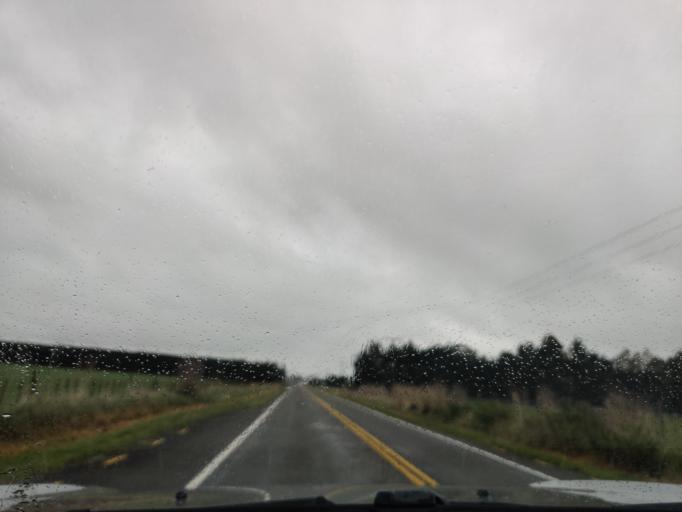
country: NZ
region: Hawke's Bay
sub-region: Hastings District
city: Hastings
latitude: -40.0172
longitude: 176.3513
